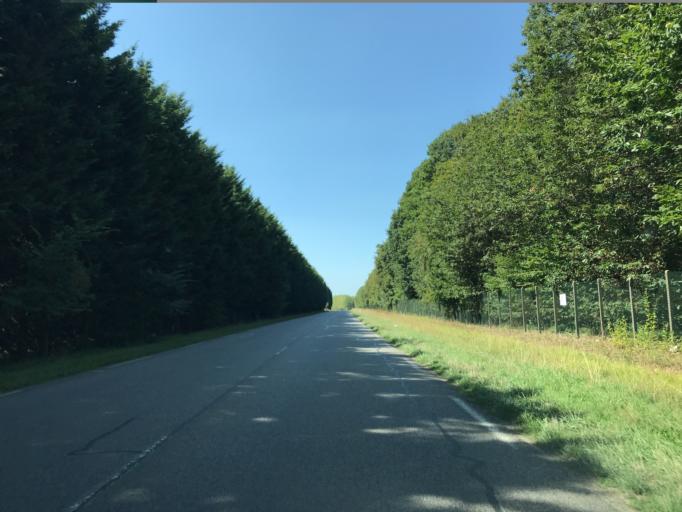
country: FR
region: Haute-Normandie
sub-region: Departement de l'Eure
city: Saint-Just
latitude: 49.0940
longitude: 1.4184
